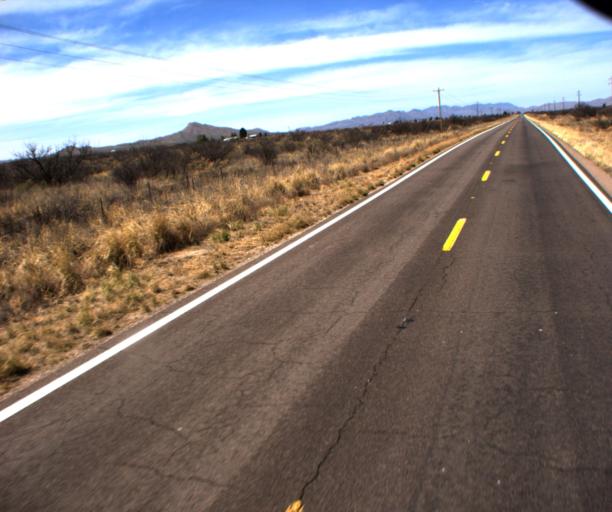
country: US
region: Arizona
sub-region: Cochise County
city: Willcox
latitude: 32.0962
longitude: -109.9092
